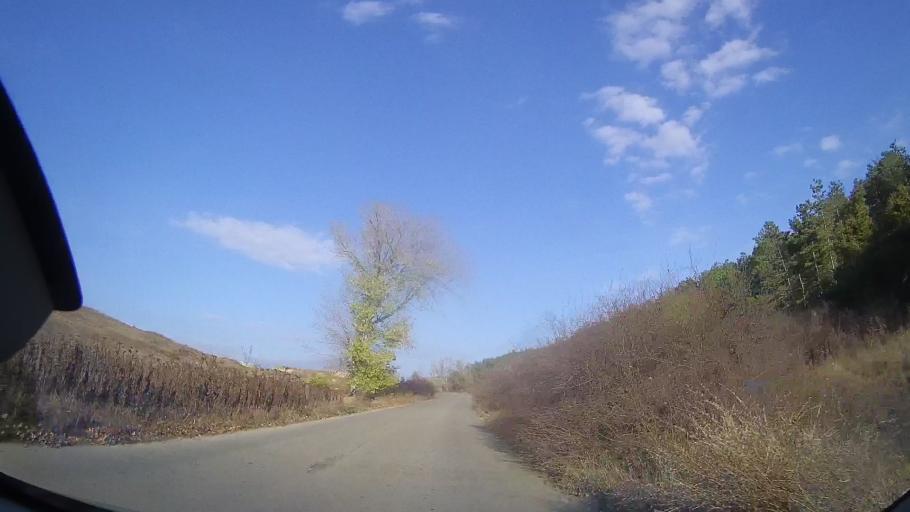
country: RO
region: Constanta
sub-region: Comuna Limanu
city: Limanu
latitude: 43.8191
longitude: 28.5188
